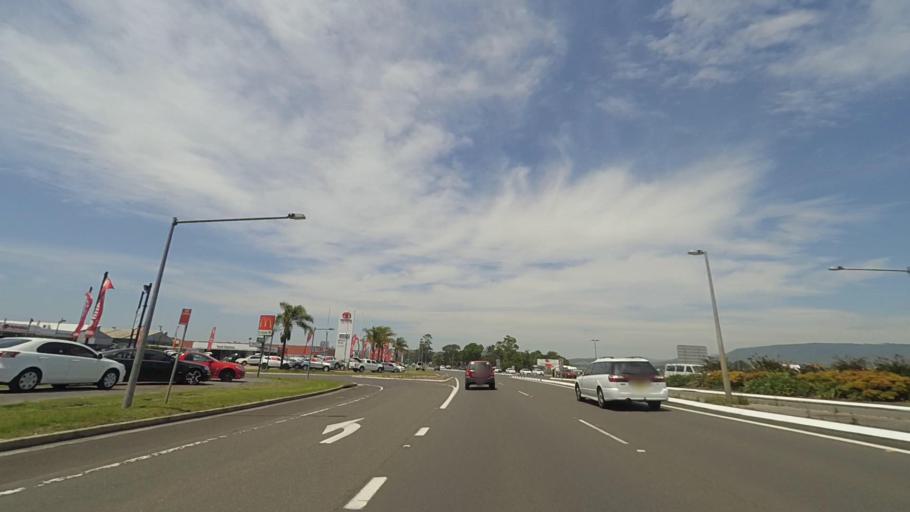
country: AU
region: New South Wales
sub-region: Shellharbour
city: Albion Park Rail
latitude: -34.5493
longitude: 150.7858
